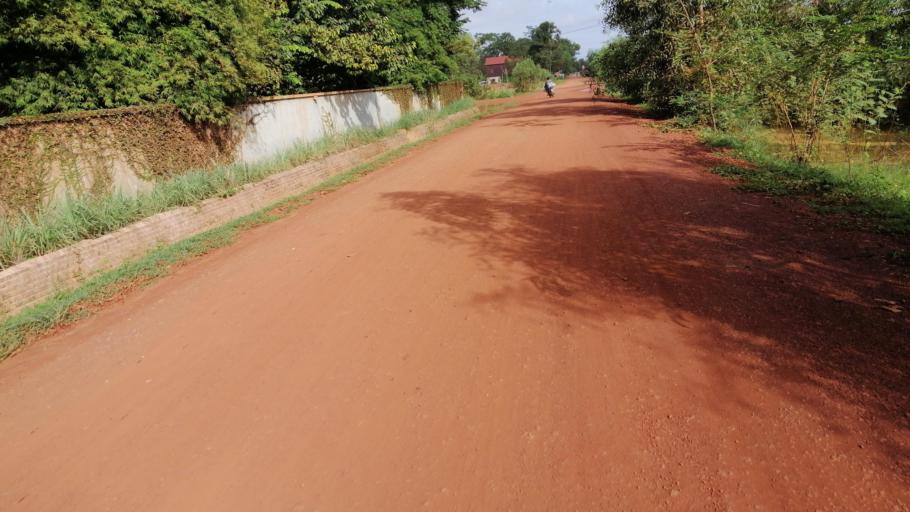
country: KH
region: Siem Reap
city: Siem Reap
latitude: 13.3588
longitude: 103.8281
